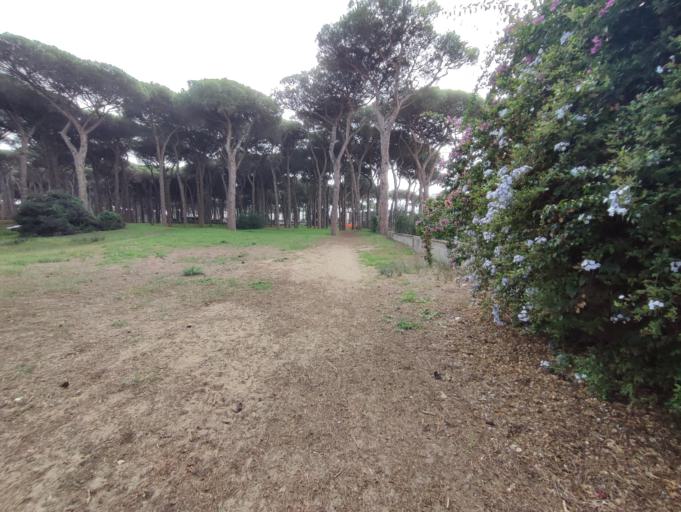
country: IT
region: Latium
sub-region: Citta metropolitana di Roma Capitale
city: Lido di Ostia
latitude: 41.7337
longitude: 12.2957
